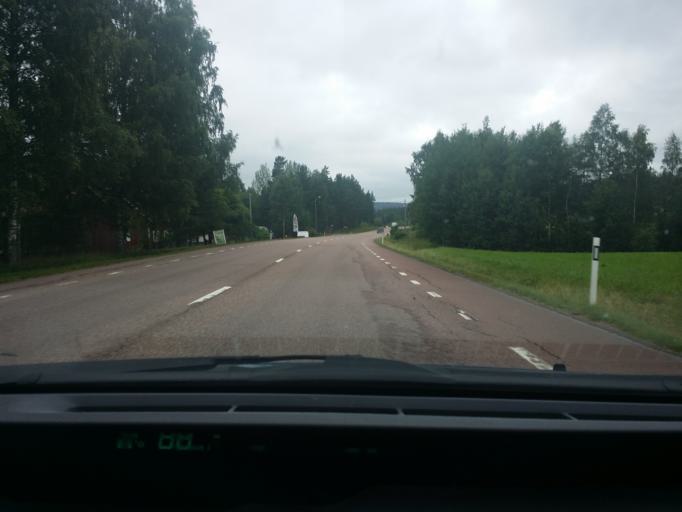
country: SE
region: Dalarna
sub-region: Gagnefs Kommun
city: Djuras
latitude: 60.5513
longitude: 15.2593
